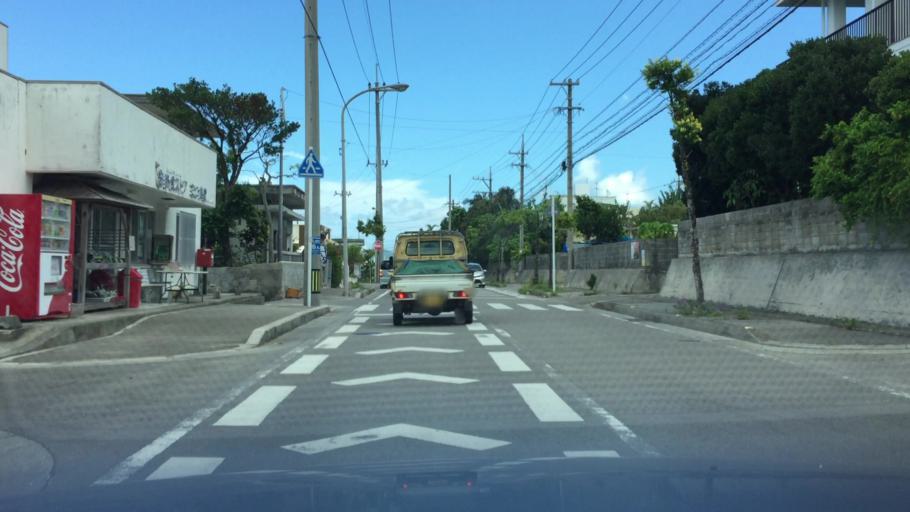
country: JP
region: Okinawa
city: Ishigaki
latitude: 24.4476
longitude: 124.1556
